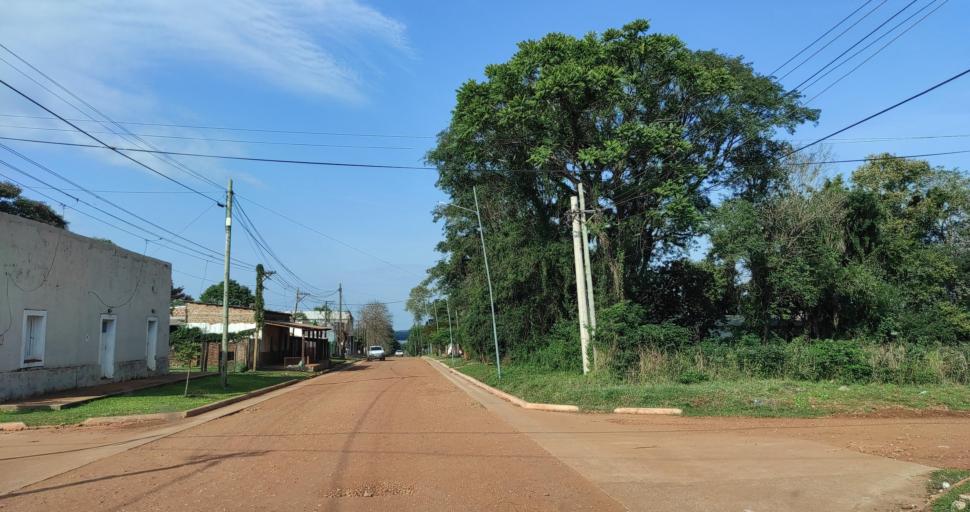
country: AR
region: Corrientes
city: Santo Tome
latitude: -28.5517
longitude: -56.0318
